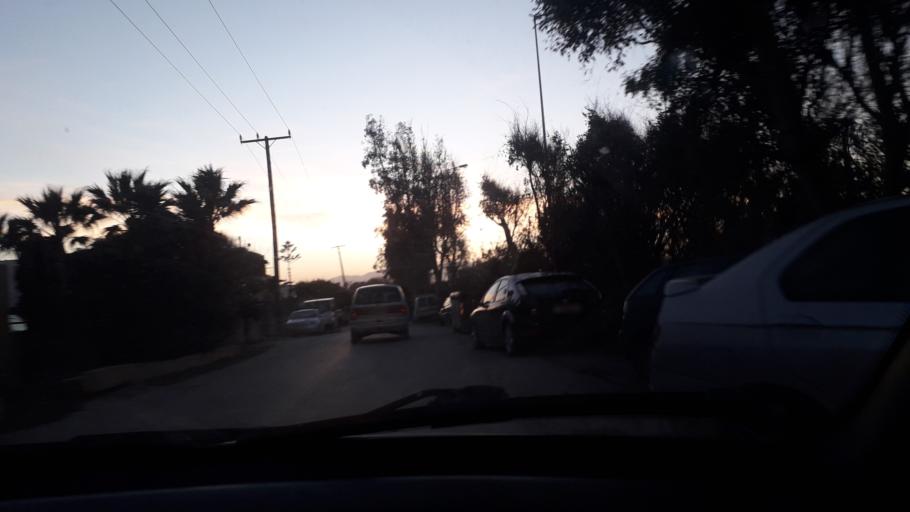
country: GR
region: Crete
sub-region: Nomos Rethymnis
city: Panormos
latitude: 35.3839
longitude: 24.5916
